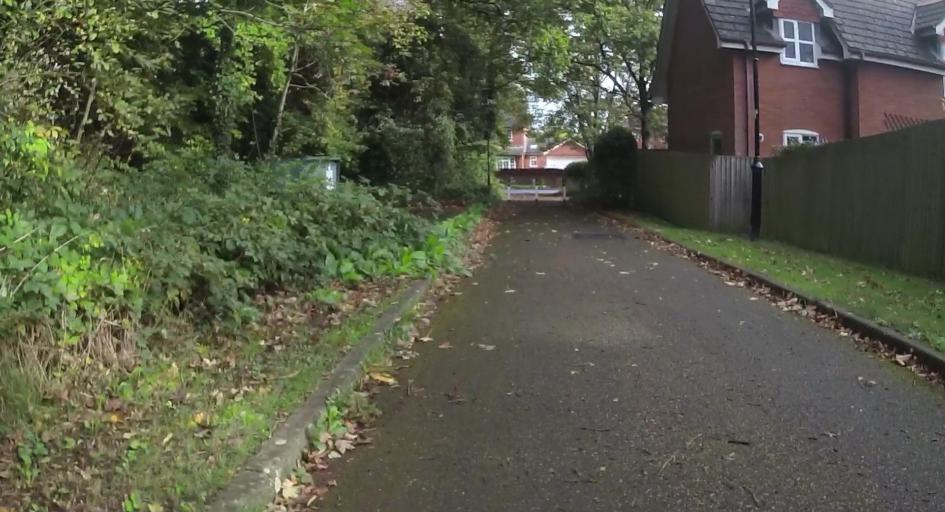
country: GB
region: England
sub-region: Hampshire
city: Odiham
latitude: 51.2847
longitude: -0.9026
